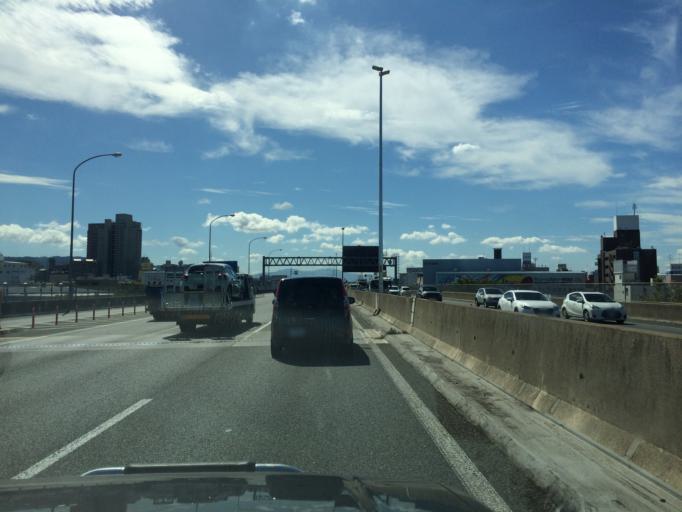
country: JP
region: Osaka
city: Daitocho
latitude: 34.6873
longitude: 135.5945
